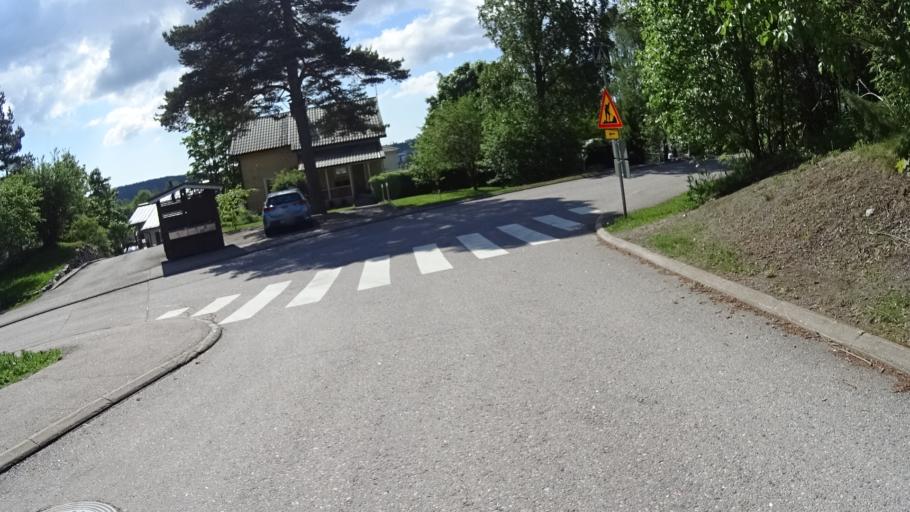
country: FI
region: Uusimaa
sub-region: Helsinki
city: Espoo
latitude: 60.2236
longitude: 24.6561
